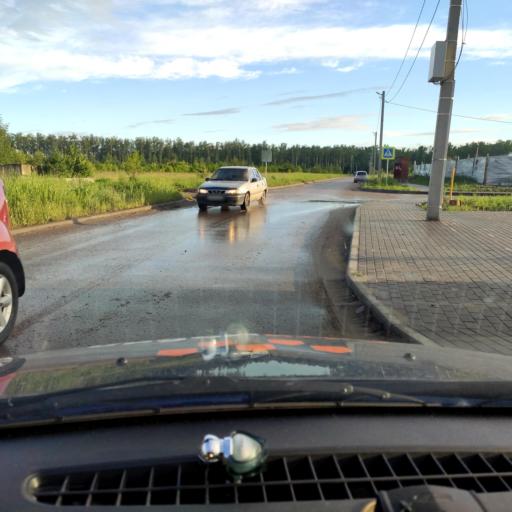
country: RU
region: Voronezj
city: Podgornoye
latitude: 51.7884
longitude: 39.1907
